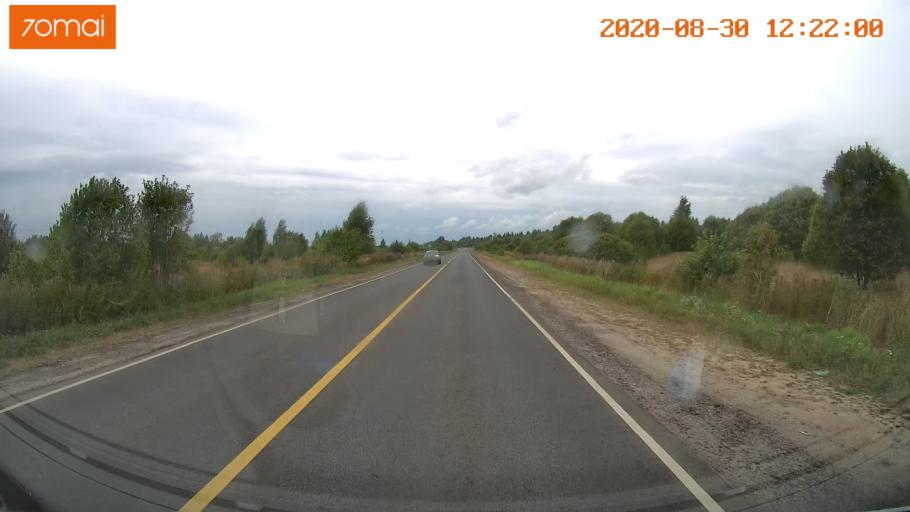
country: RU
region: Ivanovo
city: Yur'yevets
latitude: 57.3279
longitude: 42.8614
